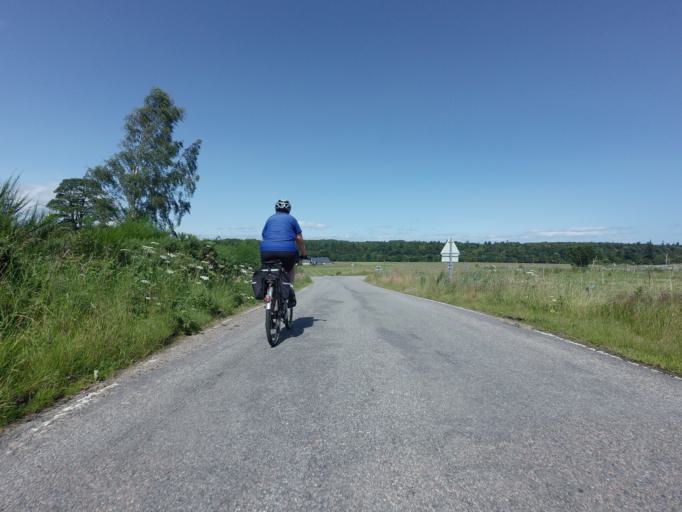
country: GB
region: Scotland
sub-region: Highland
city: Nairn
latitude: 57.5042
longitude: -3.9928
